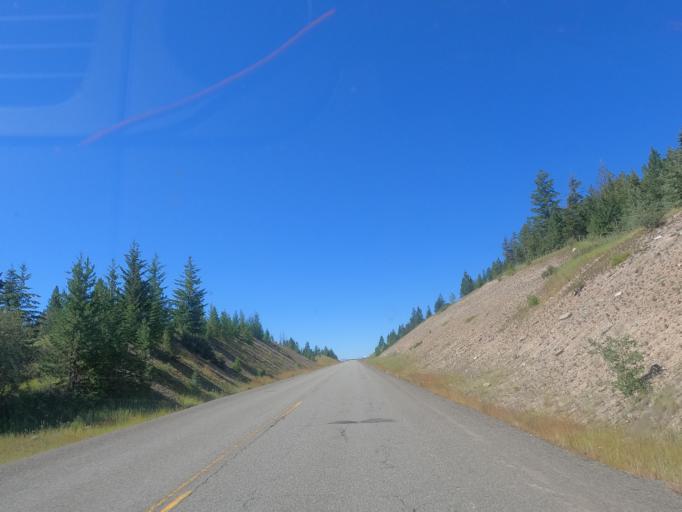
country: CA
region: British Columbia
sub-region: Thompson-Nicola Regional District
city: Ashcroft
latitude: 50.5739
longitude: -121.1739
